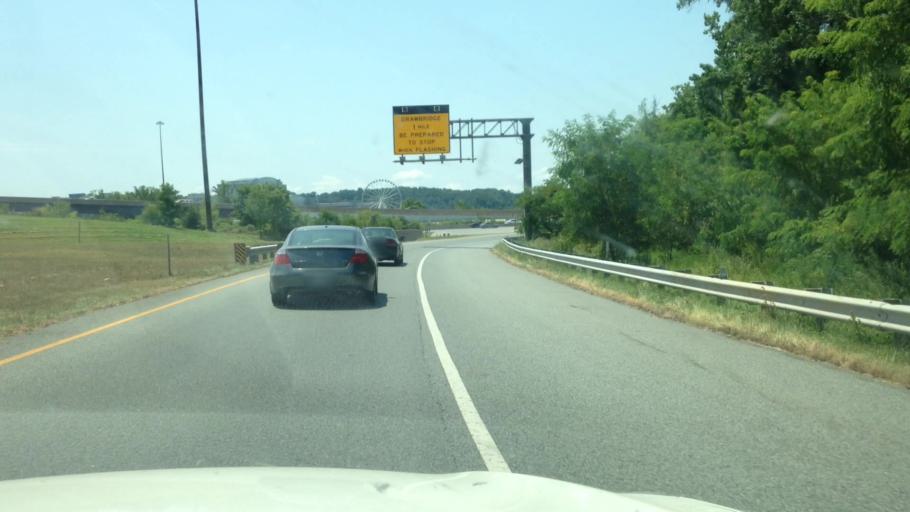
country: US
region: Maryland
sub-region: Prince George's County
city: Forest Heights
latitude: 38.7966
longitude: -77.0190
